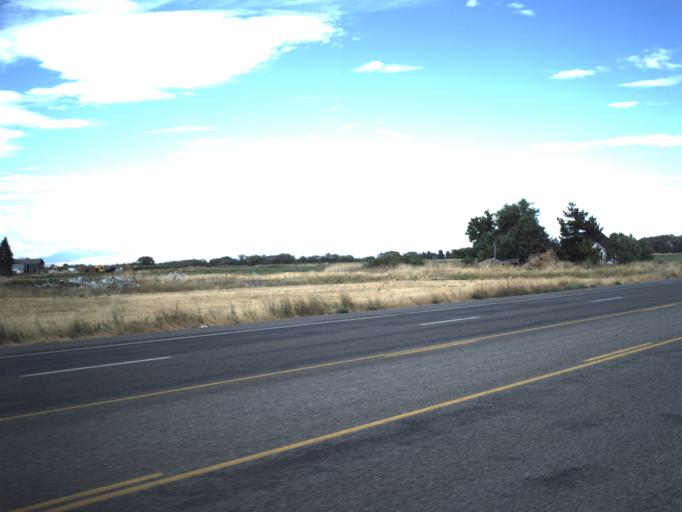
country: US
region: Utah
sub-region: Cache County
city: Wellsville
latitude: 41.6635
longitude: -111.8949
